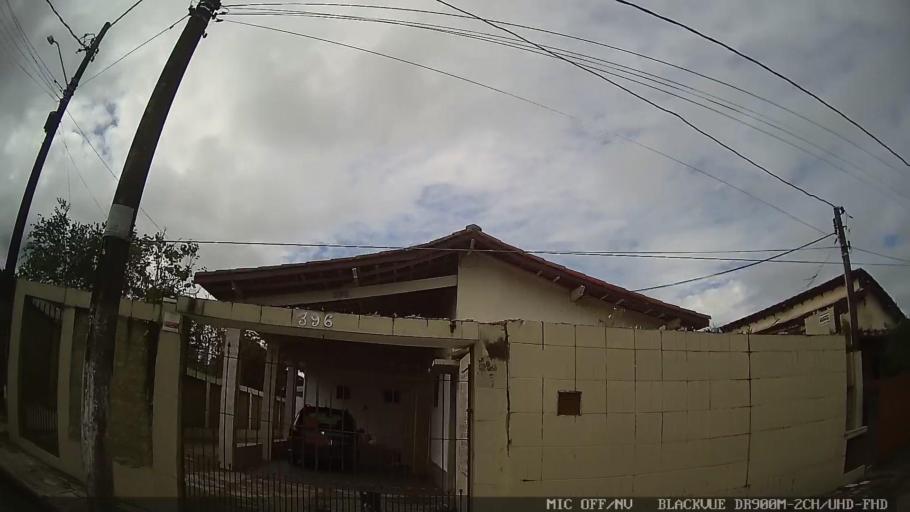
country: BR
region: Sao Paulo
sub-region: Itanhaem
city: Itanhaem
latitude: -24.1617
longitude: -46.7492
